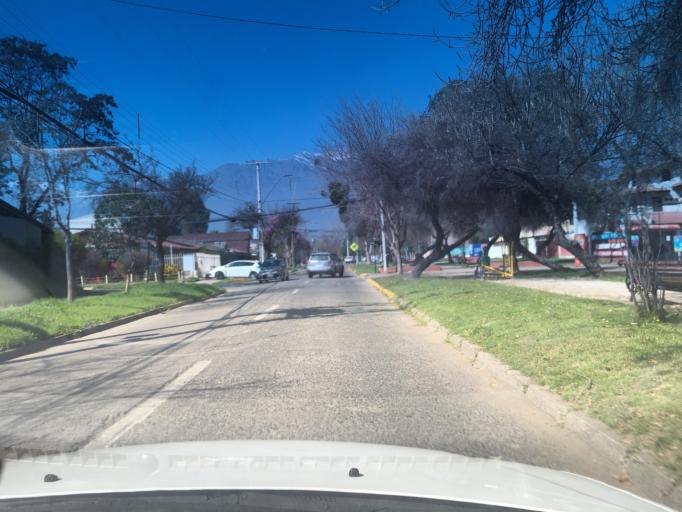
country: CL
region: Santiago Metropolitan
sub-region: Provincia de Santiago
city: Villa Presidente Frei, Nunoa, Santiago, Chile
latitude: -33.4654
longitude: -70.5791
